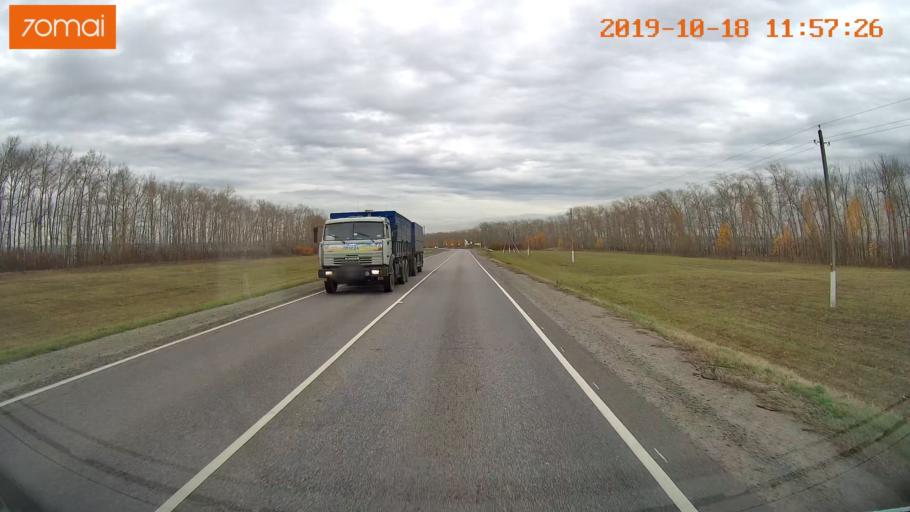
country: RU
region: Rjazan
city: Mikhaylov
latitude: 54.2664
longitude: 39.1438
